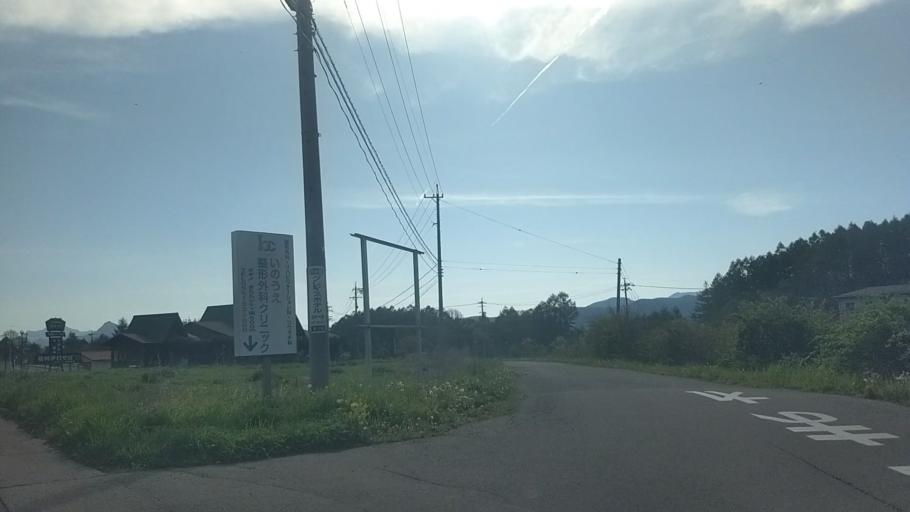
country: JP
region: Yamanashi
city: Nirasaki
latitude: 35.9450
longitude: 138.4522
